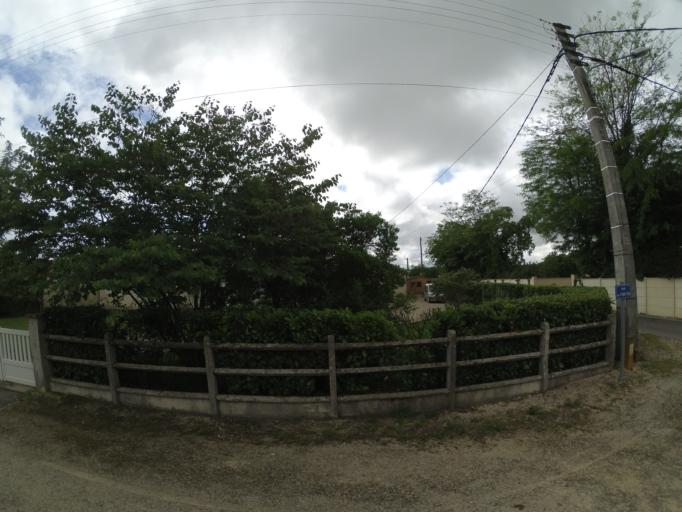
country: FR
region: Aquitaine
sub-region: Departement de la Gironde
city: Macau
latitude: 45.0108
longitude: -0.6176
